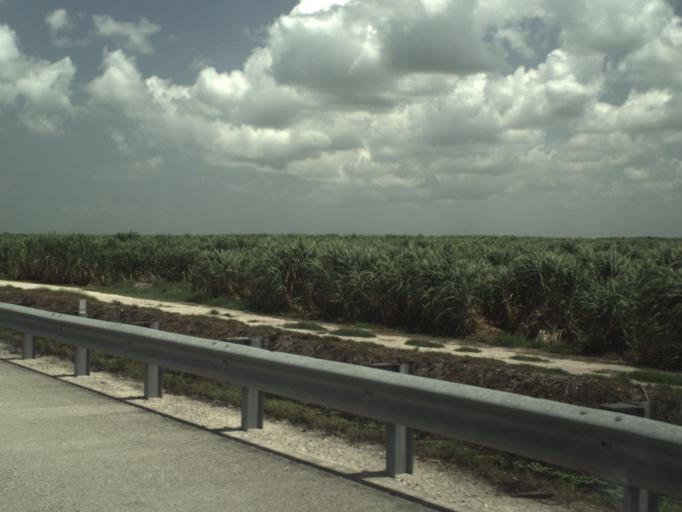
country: US
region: Florida
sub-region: Palm Beach County
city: Belle Glade
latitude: 26.7489
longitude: -80.6598
